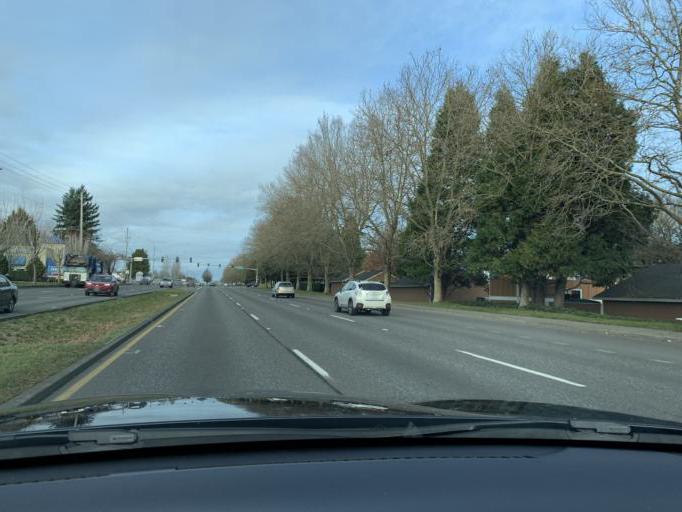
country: US
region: Washington
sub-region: Clark County
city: Mill Plain
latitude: 45.5988
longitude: -122.5038
